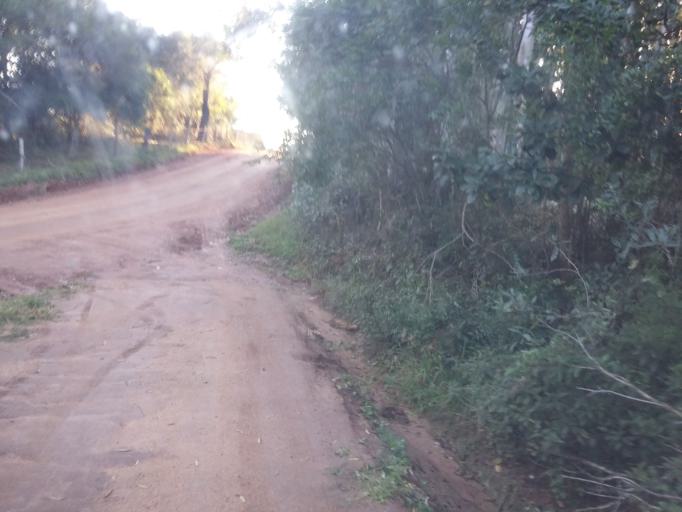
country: BR
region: Rio Grande do Sul
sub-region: Camaqua
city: Camaqua
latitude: -30.7055
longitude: -51.7684
